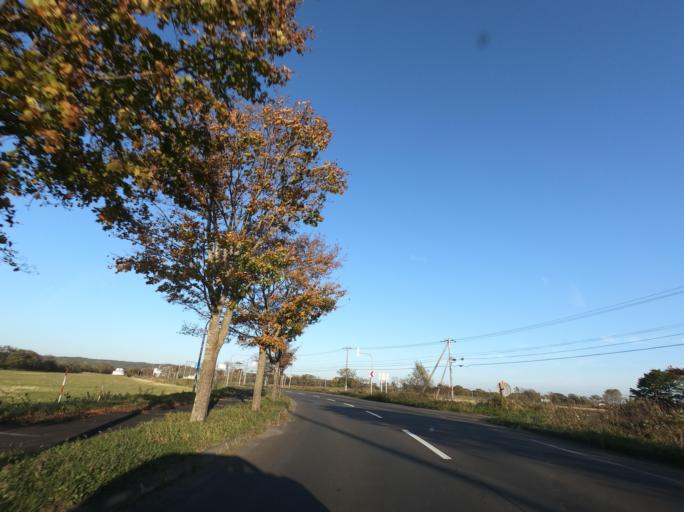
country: JP
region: Hokkaido
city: Kushiro
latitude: 43.0715
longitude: 144.2306
